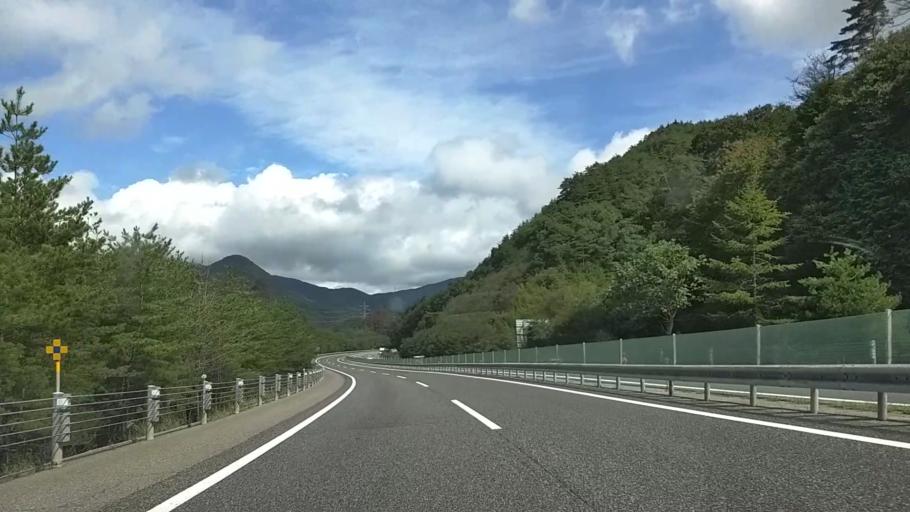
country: JP
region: Nagano
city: Omachi
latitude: 36.4420
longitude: 138.0395
